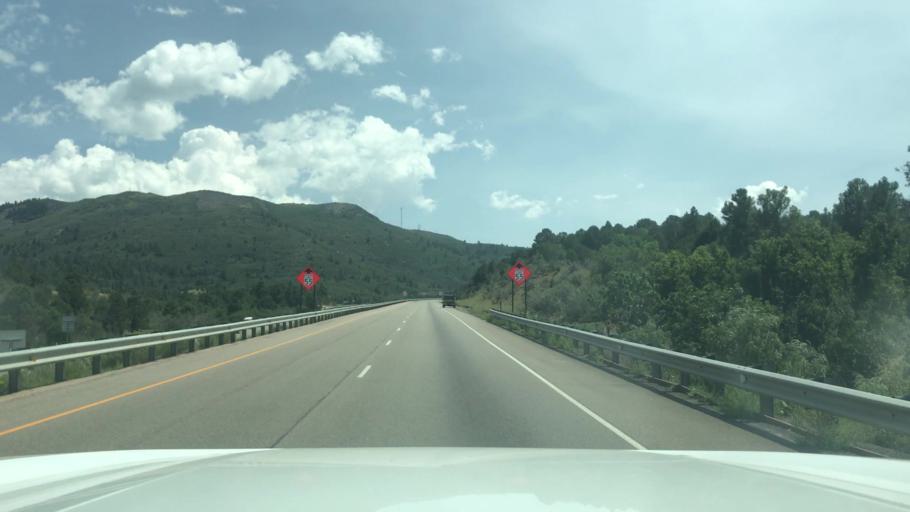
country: US
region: New Mexico
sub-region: Colfax County
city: Raton
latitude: 37.0124
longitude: -104.4816
